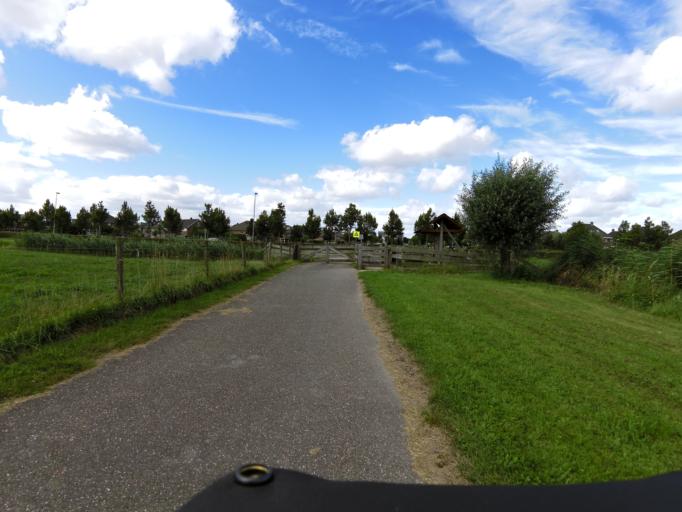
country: NL
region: South Holland
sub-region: Gemeente Barendrecht
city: Barendrecht
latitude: 51.8411
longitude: 4.5427
